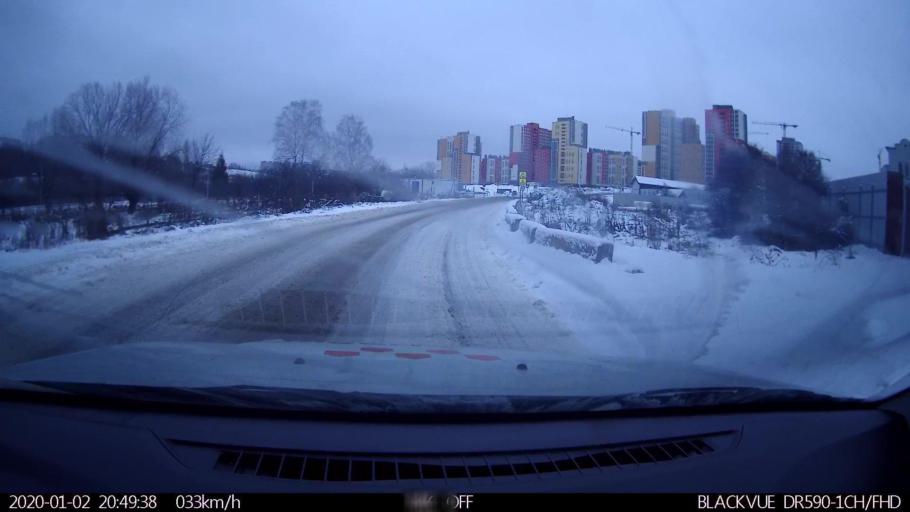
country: RU
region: Nizjnij Novgorod
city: Afonino
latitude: 56.2794
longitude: 44.0404
